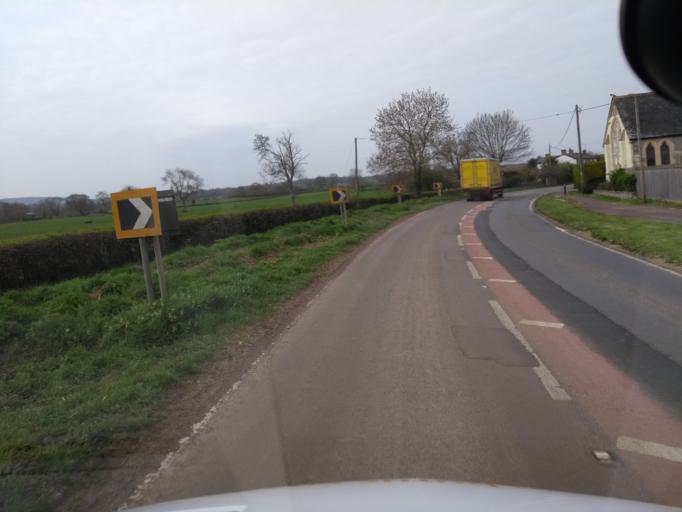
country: GB
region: England
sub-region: Somerset
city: Creech Saint Michael
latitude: 50.9962
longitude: -2.9902
